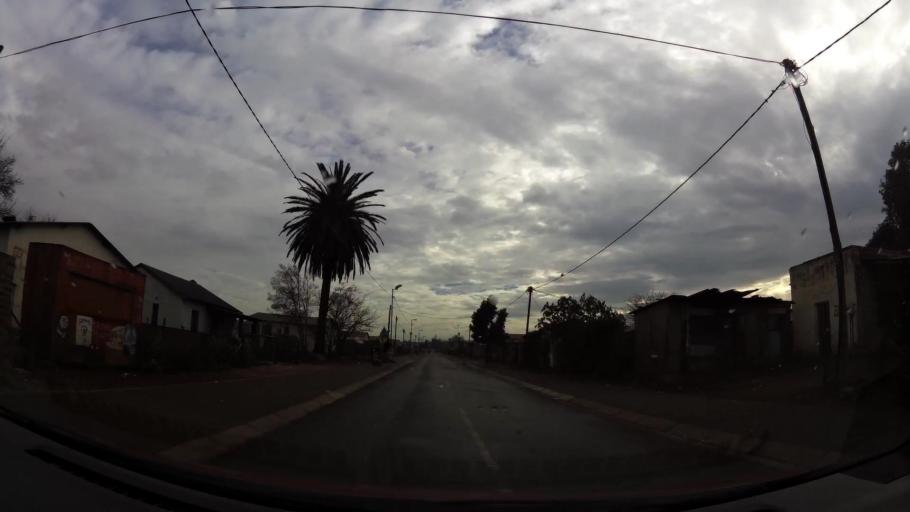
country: ZA
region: Gauteng
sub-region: City of Johannesburg Metropolitan Municipality
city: Soweto
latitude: -26.2839
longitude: 27.8420
